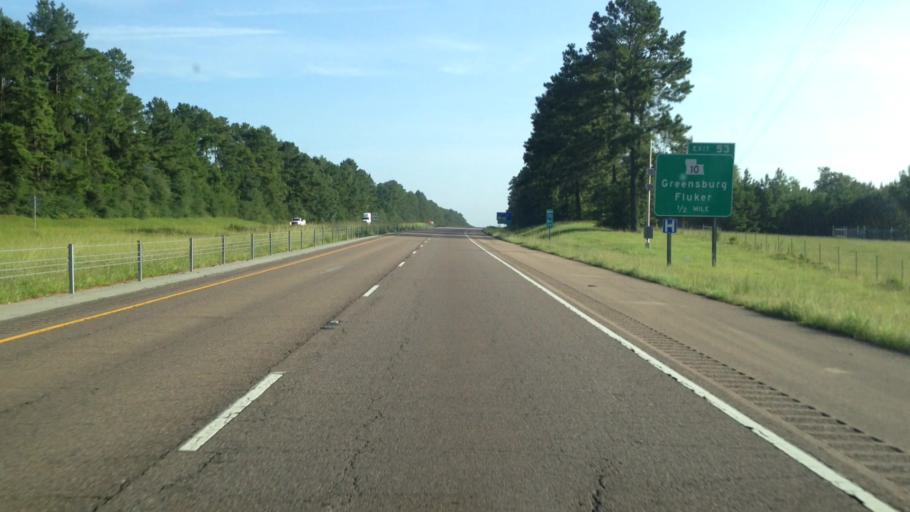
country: US
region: Louisiana
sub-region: Tangipahoa Parish
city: Roseland
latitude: 30.8141
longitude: -90.5328
